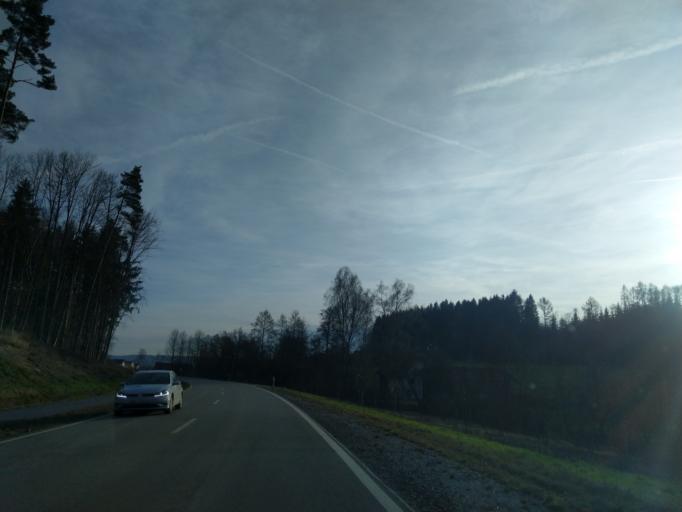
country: DE
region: Bavaria
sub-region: Lower Bavaria
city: Wallerfing
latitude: 48.6599
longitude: 12.8764
